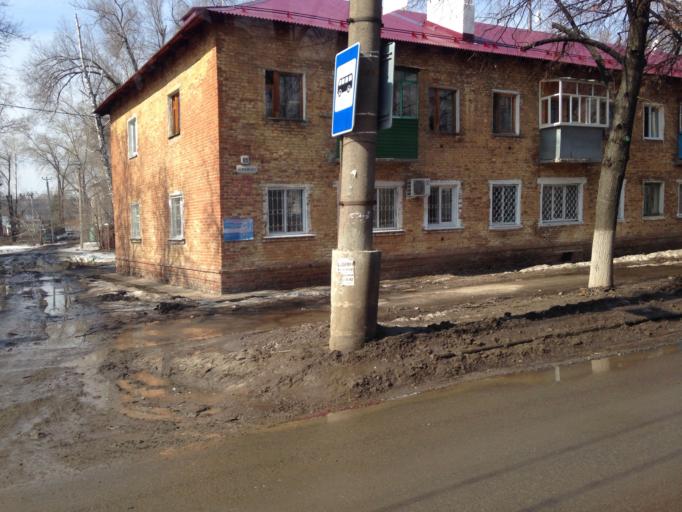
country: RU
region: Ulyanovsk
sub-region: Ulyanovskiy Rayon
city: Ulyanovsk
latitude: 54.3496
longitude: 48.5481
